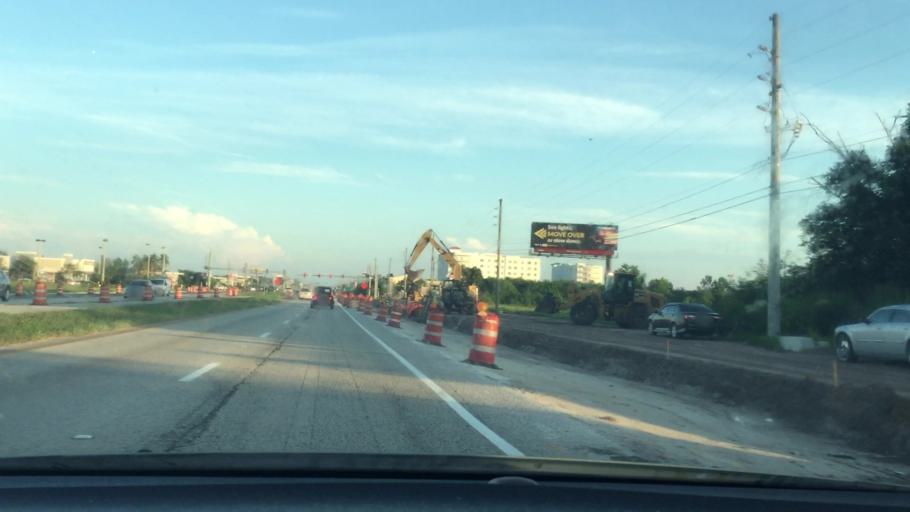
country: US
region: Florida
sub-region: Osceola County
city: Buenaventura Lakes
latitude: 28.2800
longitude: -81.3448
